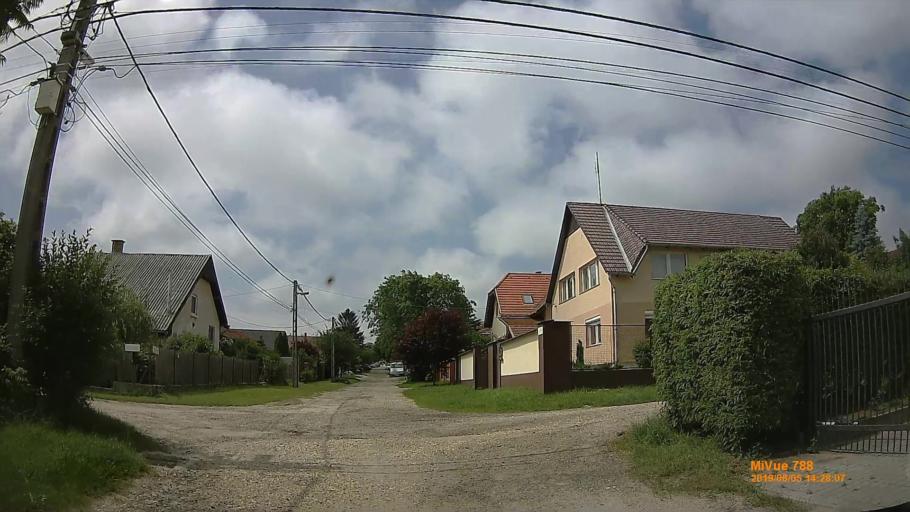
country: HU
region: Pest
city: Kistarcsa
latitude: 47.5625
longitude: 19.2615
